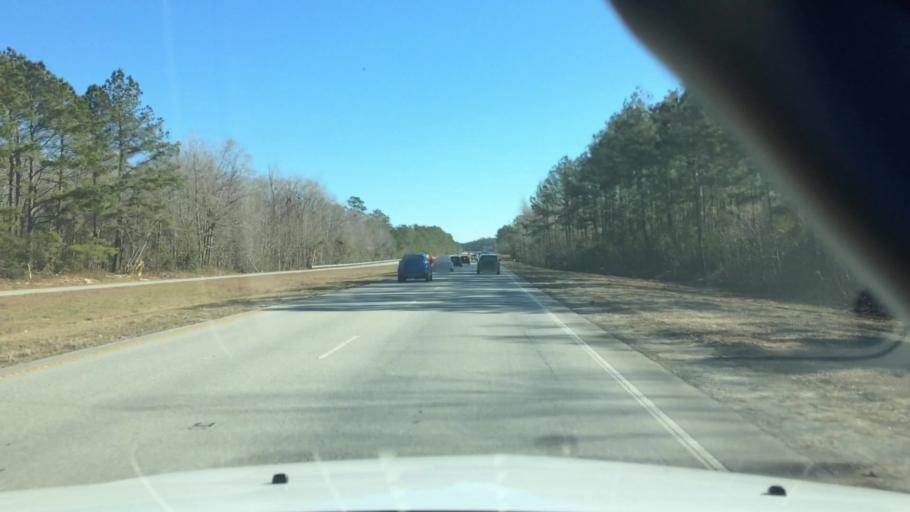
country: US
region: North Carolina
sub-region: Brunswick County
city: Bolivia
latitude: 34.0634
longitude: -78.1963
